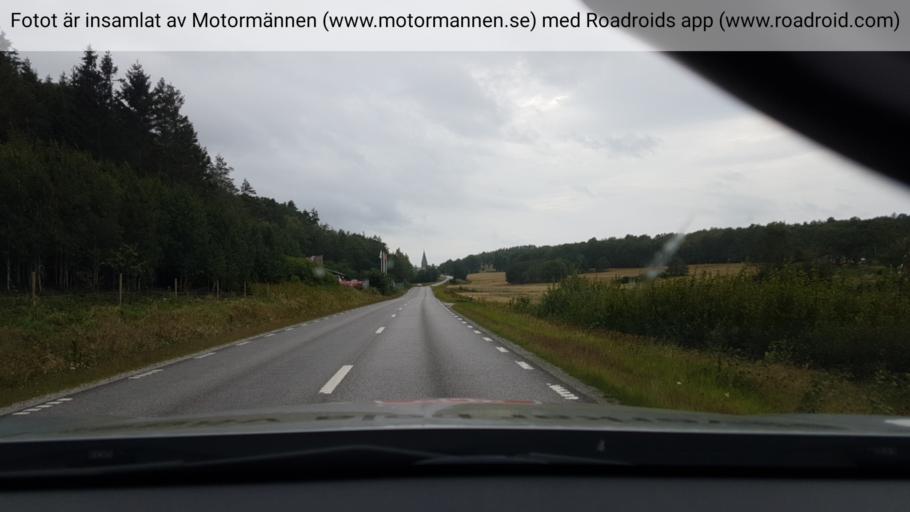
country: SE
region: Vaestra Goetaland
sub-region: Tanums Kommun
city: Grebbestad
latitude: 58.7044
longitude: 11.2587
